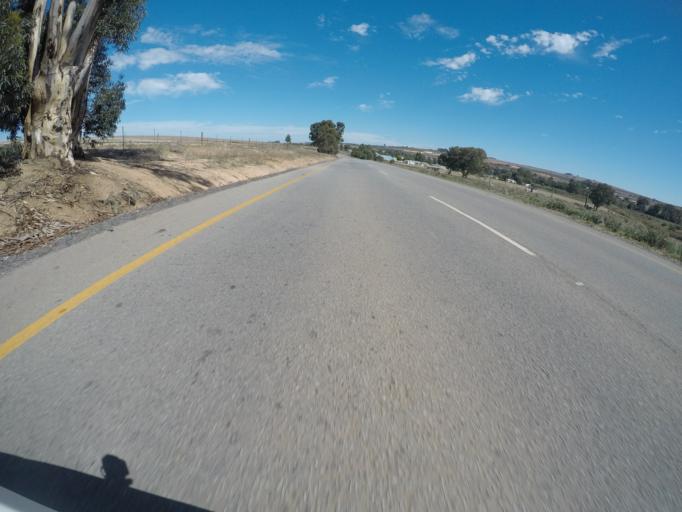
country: ZA
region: Western Cape
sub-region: West Coast District Municipality
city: Malmesbury
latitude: -33.4841
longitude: 18.6933
